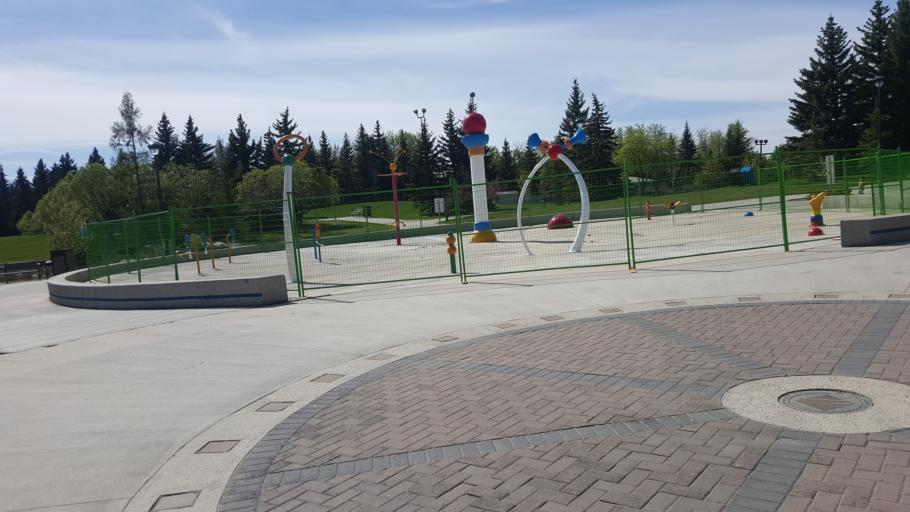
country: CA
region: Saskatchewan
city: Lloydminster
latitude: 53.2612
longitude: -110.0391
